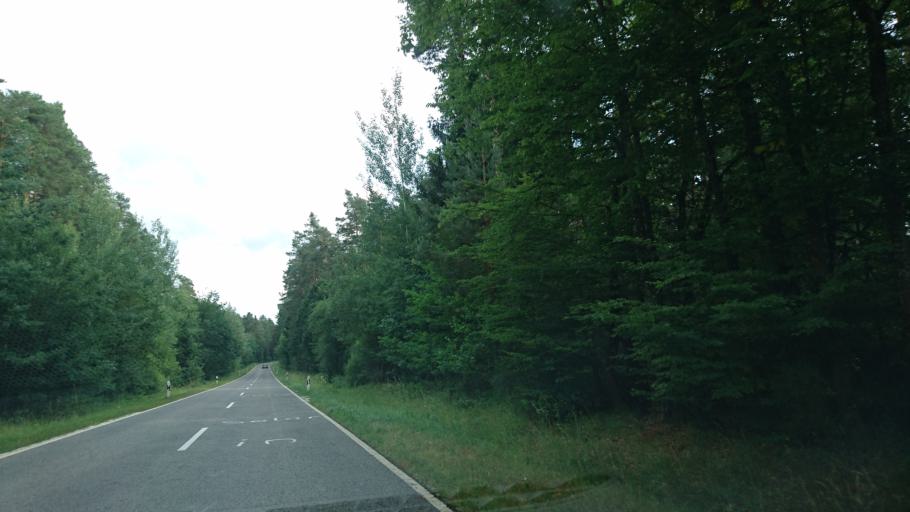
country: DE
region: Bavaria
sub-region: Regierungsbezirk Mittelfranken
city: Heideck
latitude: 49.1715
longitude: 11.1184
